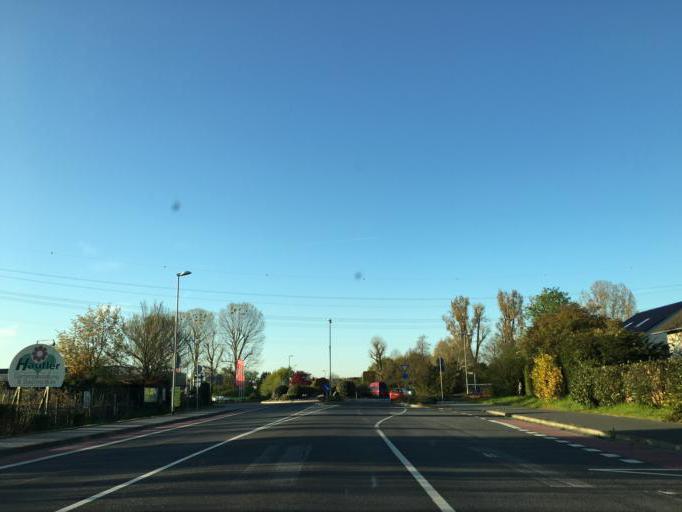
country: DE
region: Hesse
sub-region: Regierungsbezirk Darmstadt
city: Rodgau
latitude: 50.0137
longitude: 8.8906
